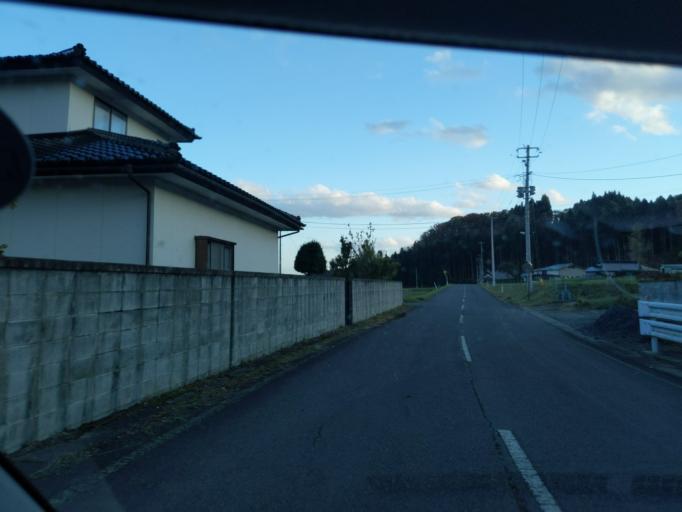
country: JP
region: Iwate
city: Mizusawa
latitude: 39.0424
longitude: 141.0505
